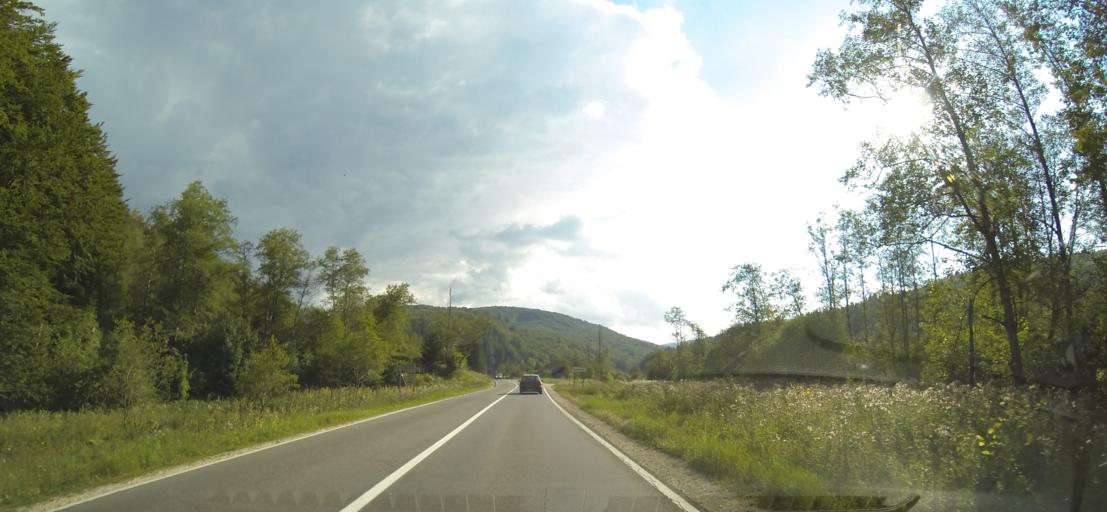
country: RO
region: Brasov
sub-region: Comuna Tarlungeni
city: Zizin
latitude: 45.5191
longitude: 25.8442
